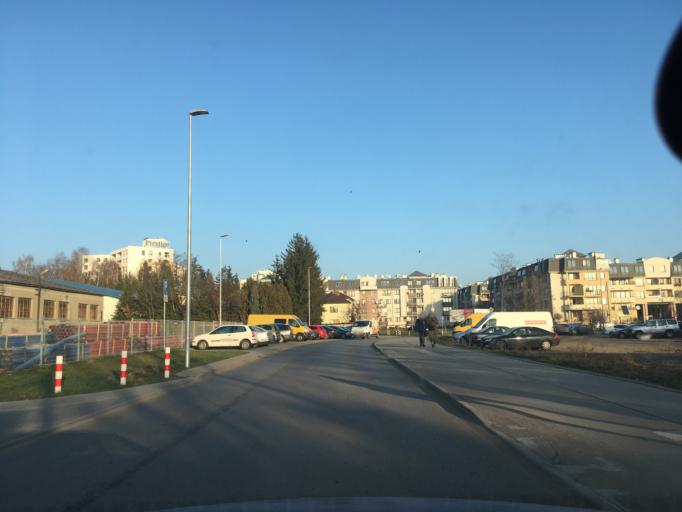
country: PL
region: Masovian Voivodeship
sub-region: Powiat piaseczynski
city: Piaseczno
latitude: 52.0752
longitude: 21.0126
